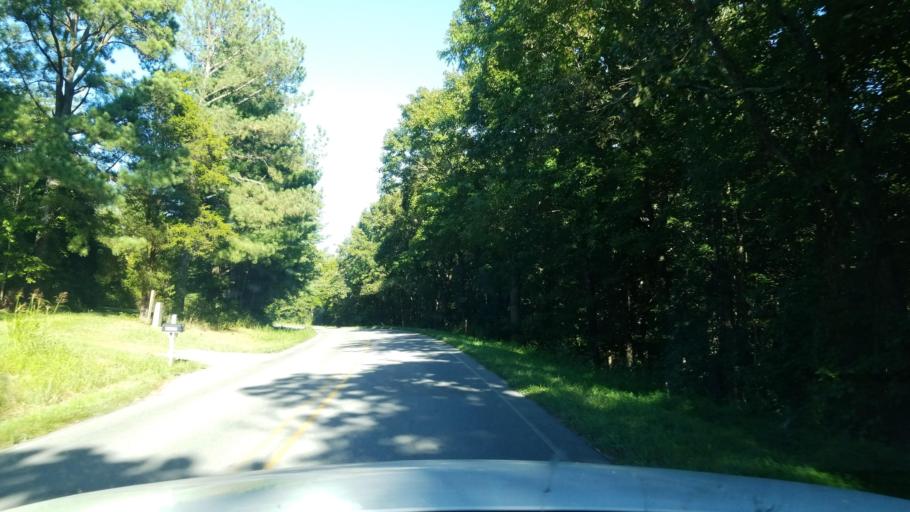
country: US
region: Illinois
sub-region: Hardin County
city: Elizabethtown
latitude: 37.5777
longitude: -88.3775
